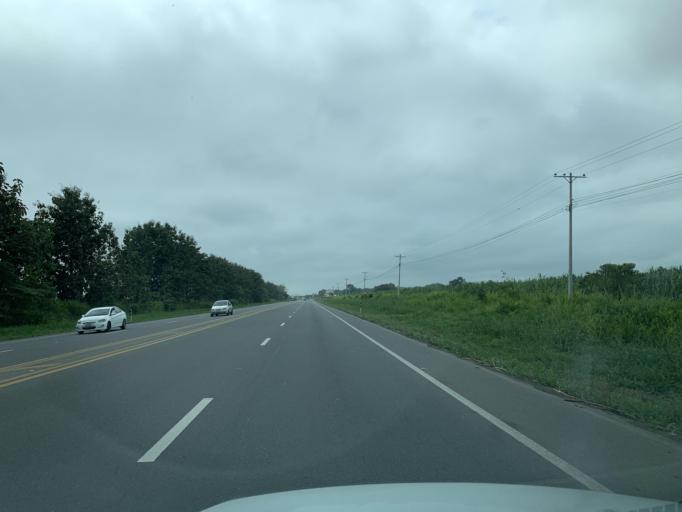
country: EC
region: Guayas
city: Coronel Marcelino Mariduena
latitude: -2.3116
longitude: -79.4755
